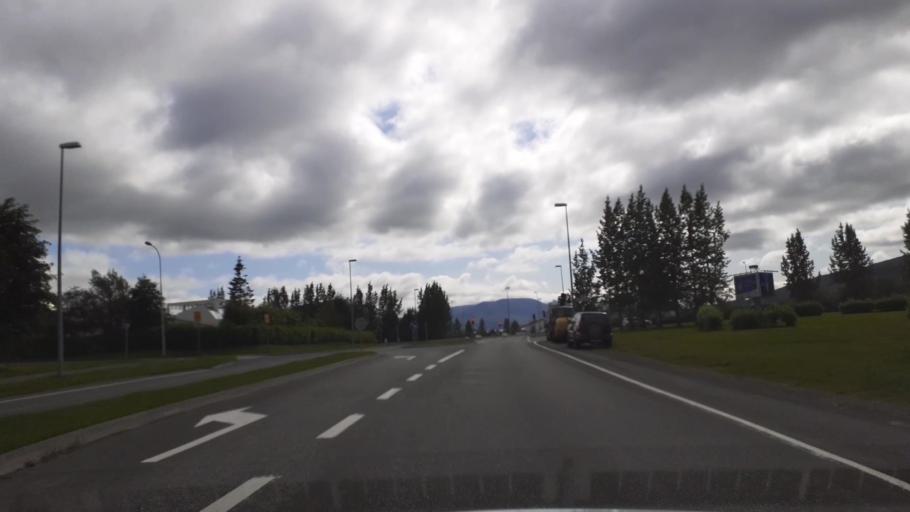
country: IS
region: Northeast
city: Akureyri
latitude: 65.6794
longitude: -18.1156
